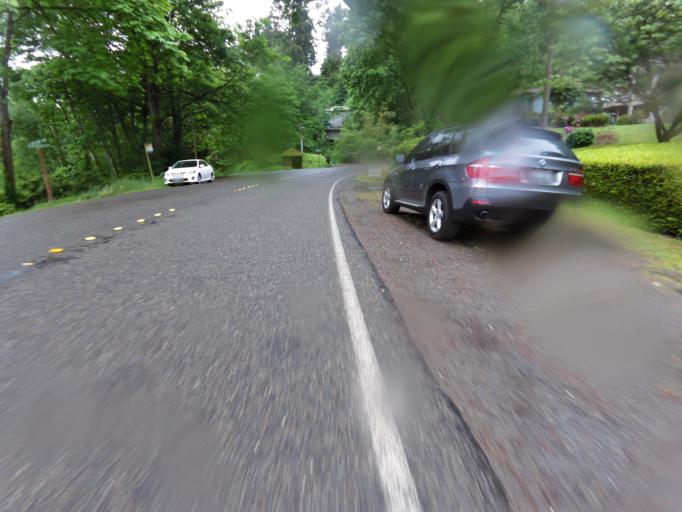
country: US
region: Washington
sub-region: King County
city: Bryn Mawr-Skyway
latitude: 47.5284
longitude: -122.2252
